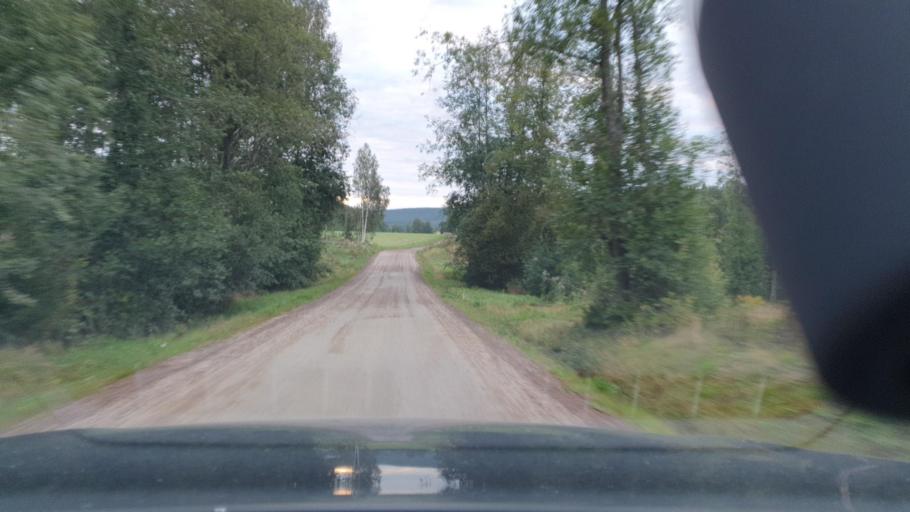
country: SE
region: Vaermland
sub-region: Munkfors Kommun
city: Munkfors
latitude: 59.8310
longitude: 13.4967
